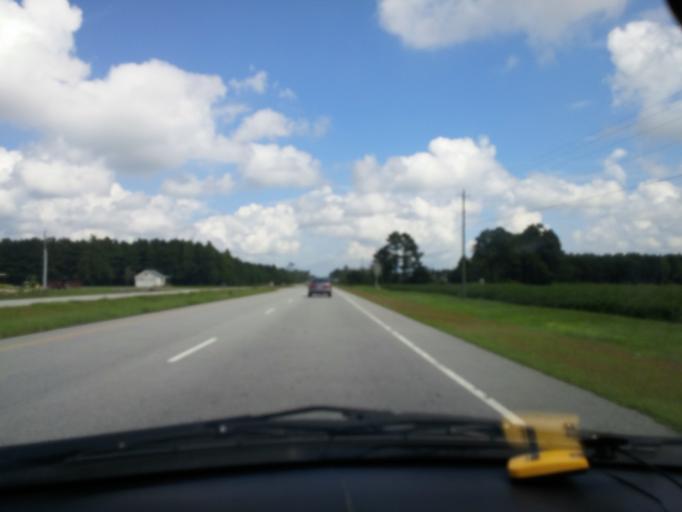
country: US
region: North Carolina
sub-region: Duplin County
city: Beulaville
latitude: 35.1001
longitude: -77.7234
